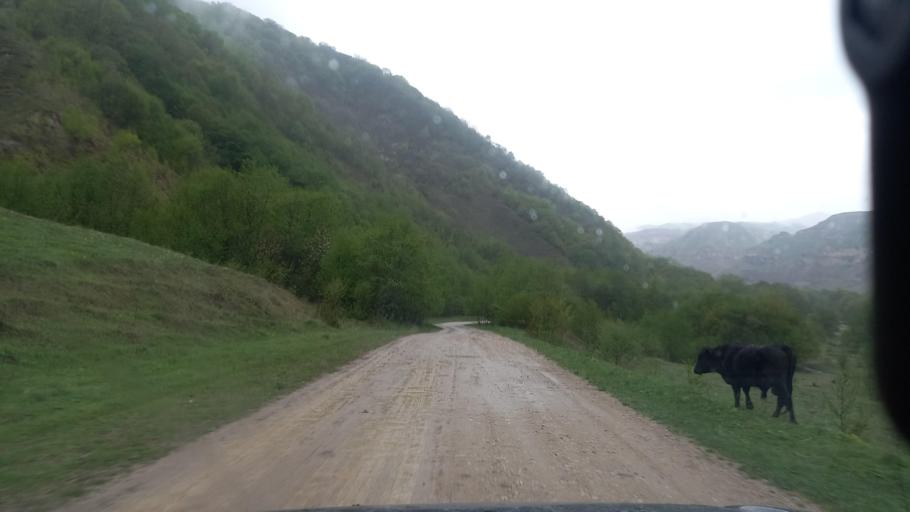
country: RU
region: Kabardino-Balkariya
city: Gundelen
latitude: 43.5872
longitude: 43.0810
